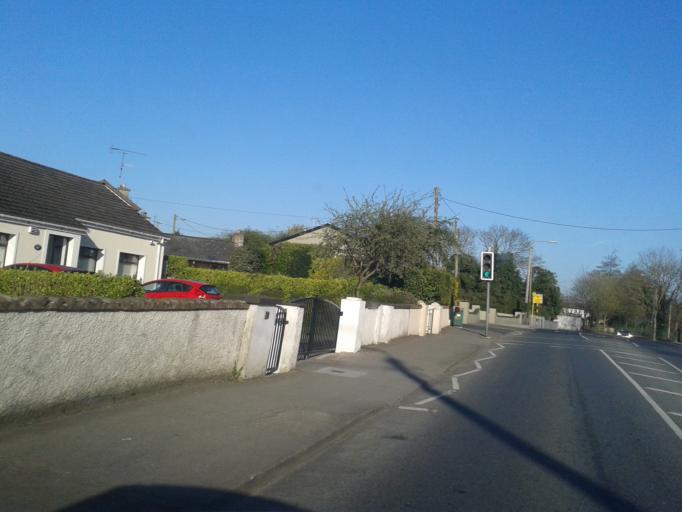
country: IE
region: Leinster
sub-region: Fingal County
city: Swords
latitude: 53.4618
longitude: -6.2301
